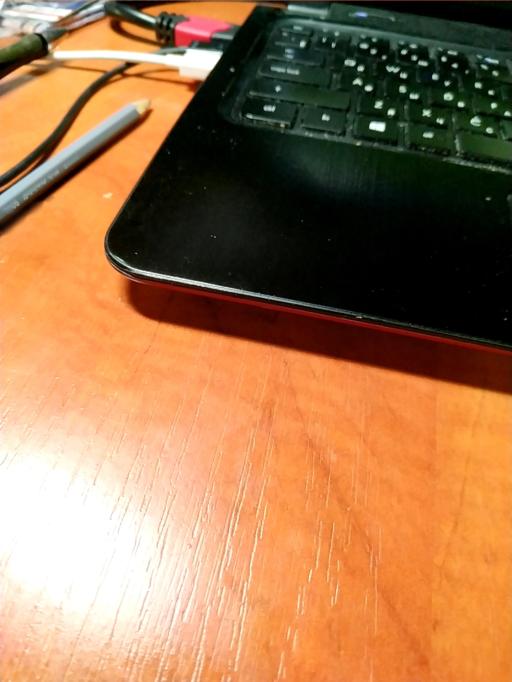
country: RU
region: Novgorod
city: Uglovka
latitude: 58.2853
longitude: 33.6063
